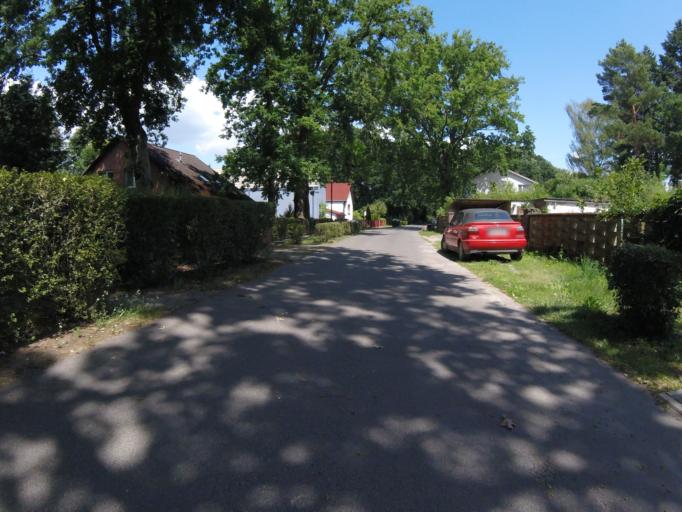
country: DE
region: Brandenburg
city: Bestensee
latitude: 52.2214
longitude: 13.6525
